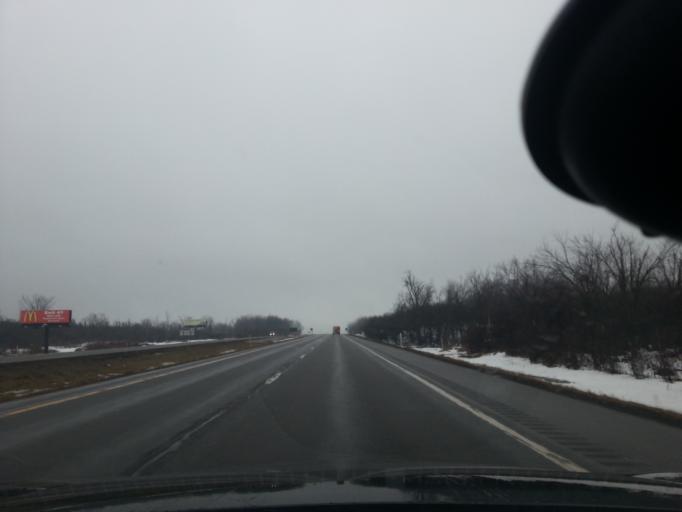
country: US
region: New York
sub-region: Jefferson County
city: Watertown
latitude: 43.9511
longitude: -75.9558
